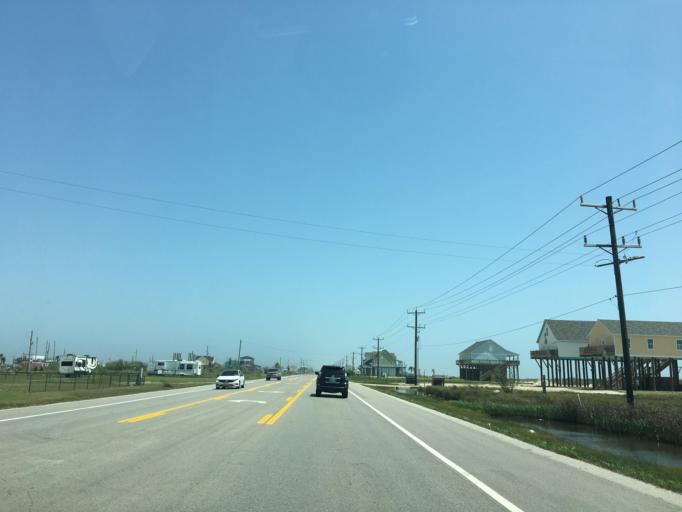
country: US
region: Texas
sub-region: Galveston County
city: Bolivar Peninsula
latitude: 29.5111
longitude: -94.4930
